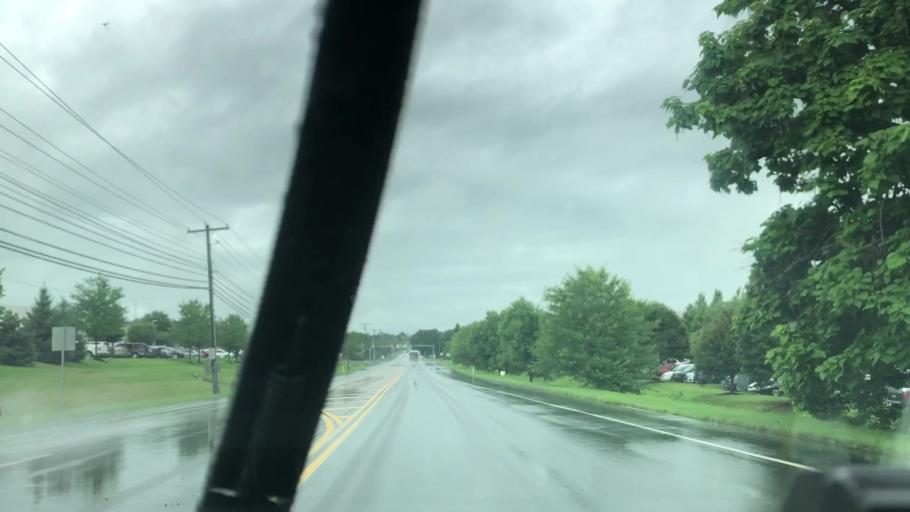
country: US
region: Pennsylvania
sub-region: Lehigh County
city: Trexlertown
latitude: 40.5884
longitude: -75.6076
